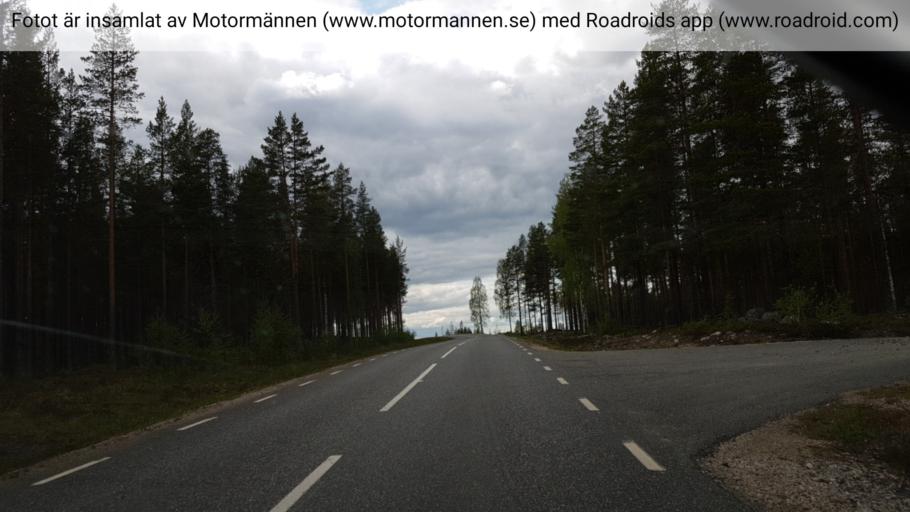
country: SE
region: Vaesterbotten
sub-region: Vindelns Kommun
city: Vindeln
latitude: 64.5224
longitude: 19.8060
